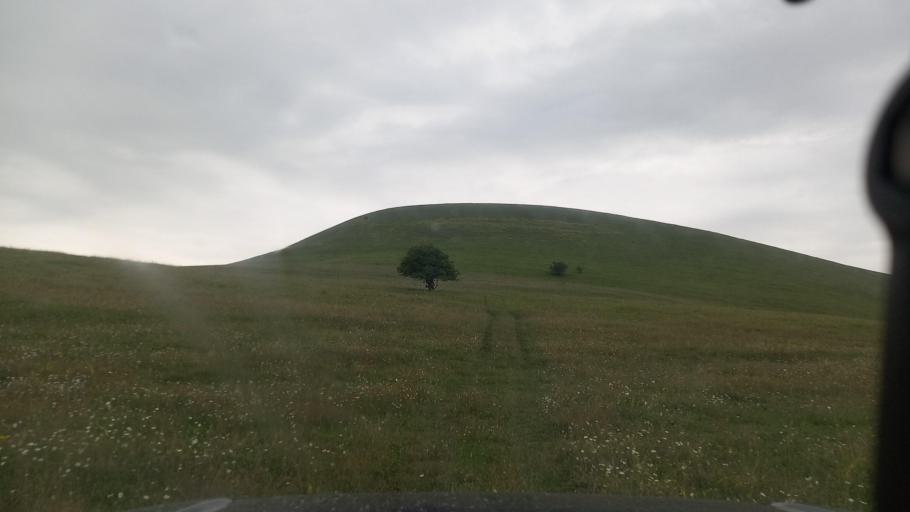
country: RU
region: Karachayevo-Cherkesiya
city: Pregradnaya
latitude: 43.9518
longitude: 41.1595
